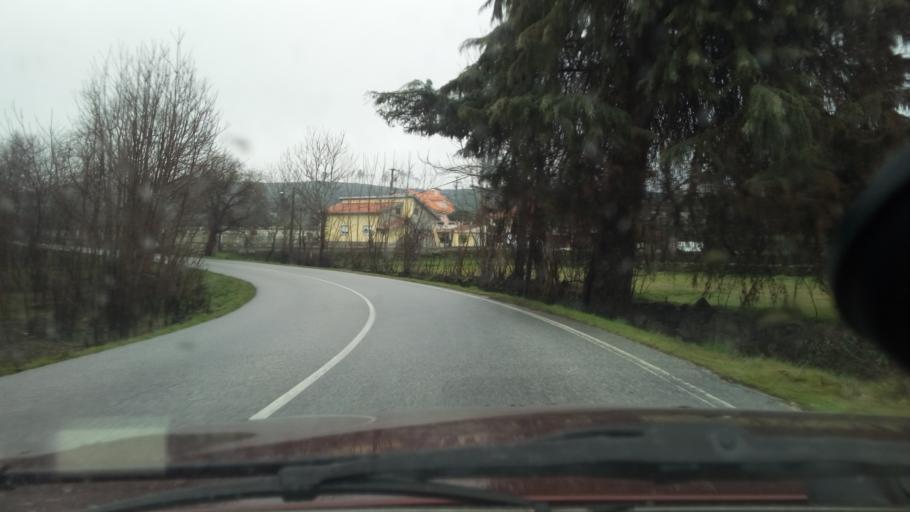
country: PT
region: Viseu
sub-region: Mangualde
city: Mangualde
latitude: 40.6061
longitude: -7.7154
